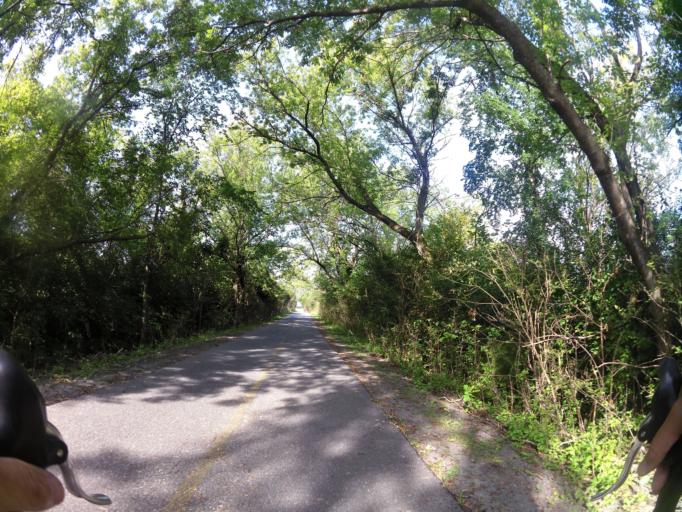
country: CA
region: Ontario
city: Bells Corners
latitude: 45.3410
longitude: -75.8618
